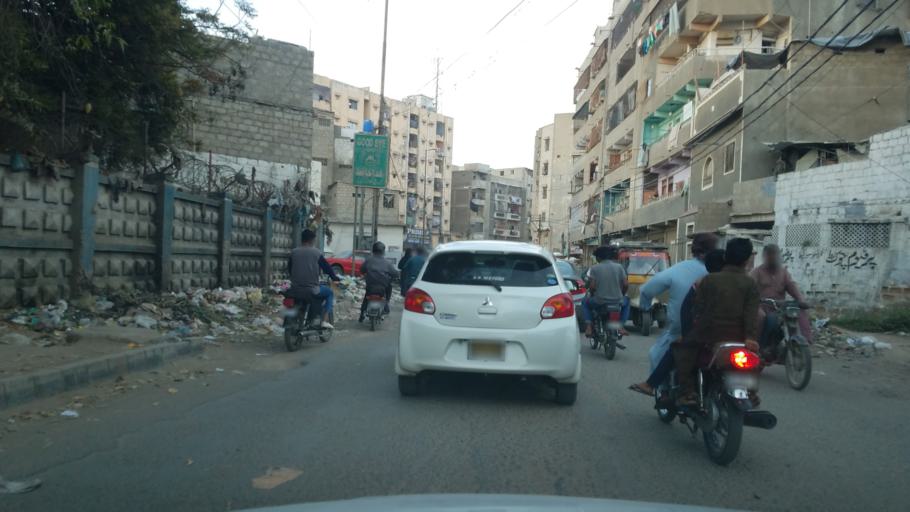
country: PK
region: Sindh
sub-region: Karachi District
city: Karachi
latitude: 24.8730
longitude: 67.0288
